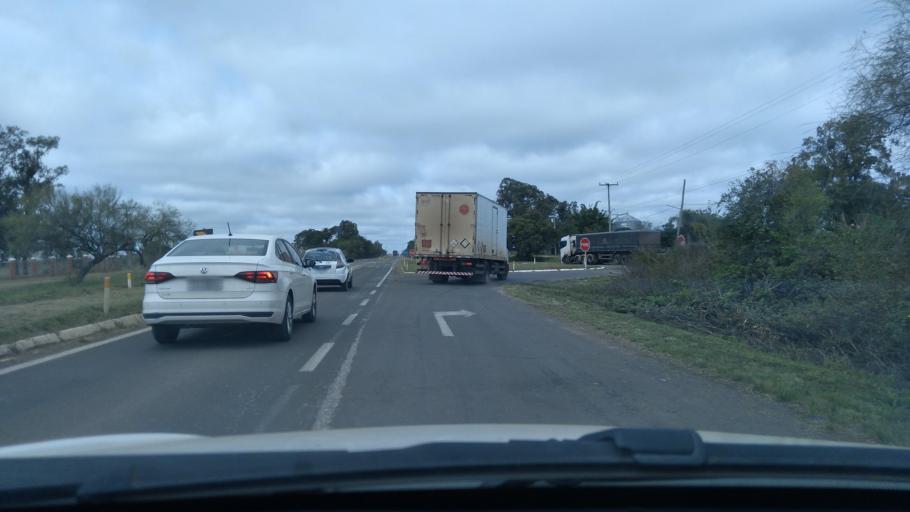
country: BR
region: Rio Grande do Sul
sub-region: Dom Pedrito
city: Dom Pedrito
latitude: -30.9835
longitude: -54.6392
